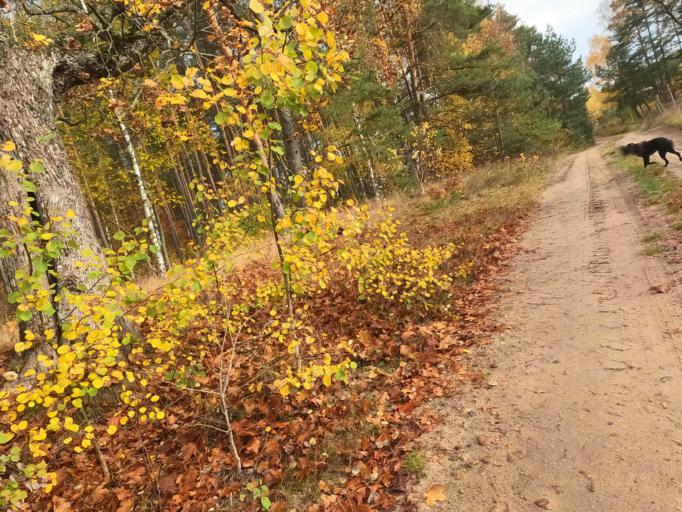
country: PL
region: West Pomeranian Voivodeship
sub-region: Powiat szczecinecki
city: Lubowo
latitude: 53.5412
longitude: 16.4359
